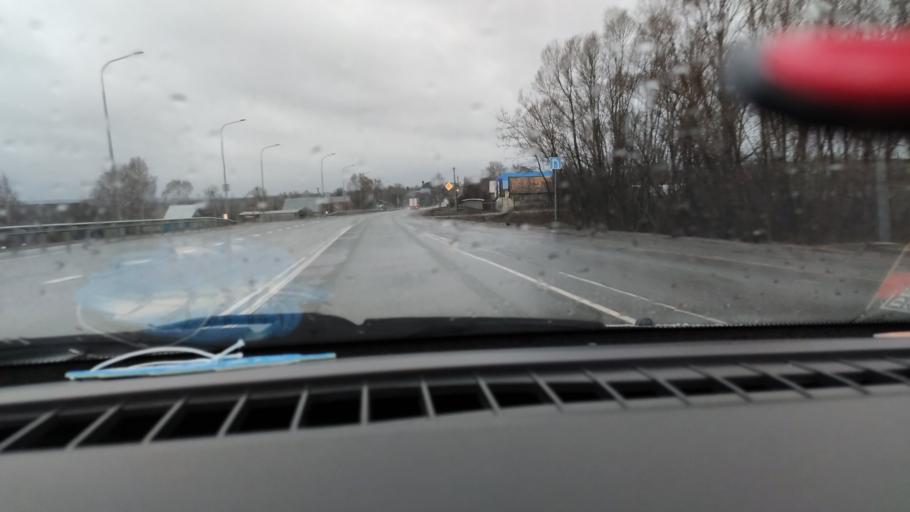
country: RU
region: Tatarstan
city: Mendeleyevsk
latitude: 56.0326
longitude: 52.3789
